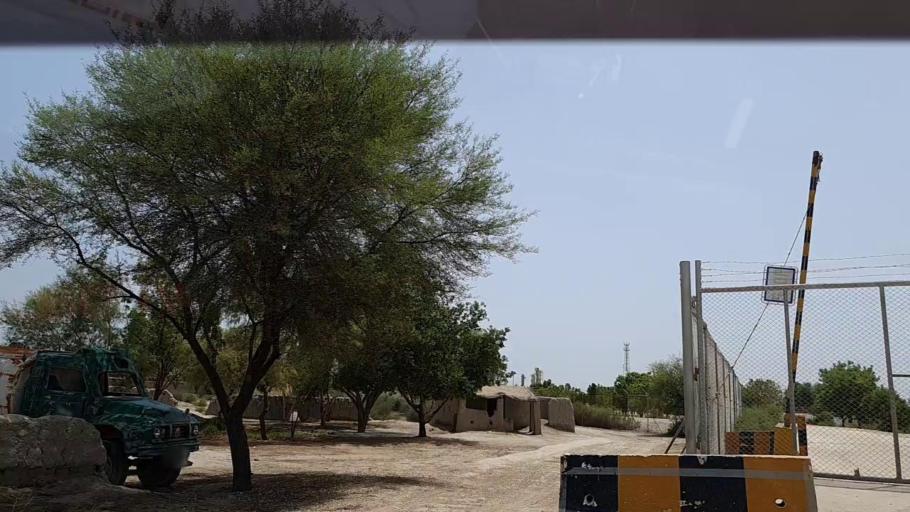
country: PK
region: Sindh
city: Johi
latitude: 26.7113
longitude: 67.6679
